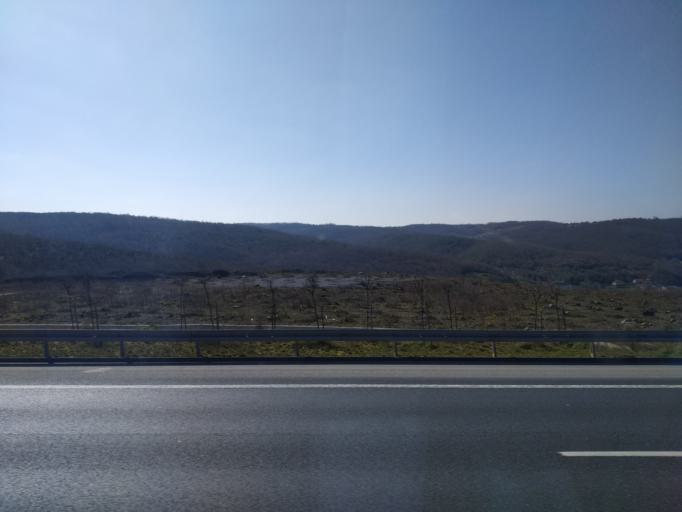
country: TR
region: Istanbul
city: Mahmut Sevket Pasa
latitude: 41.1764
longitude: 29.2402
